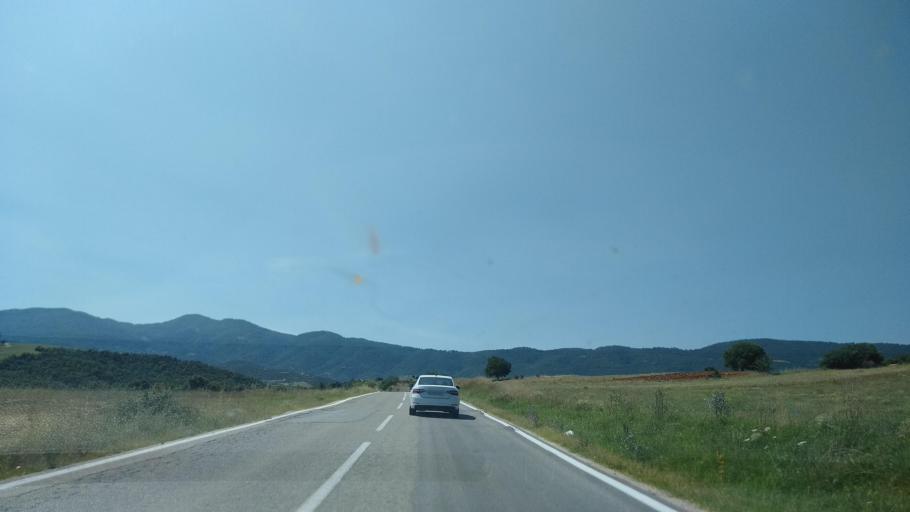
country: GR
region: Central Macedonia
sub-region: Nomos Thessalonikis
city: Nea Apollonia
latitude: 40.5226
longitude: 23.4720
